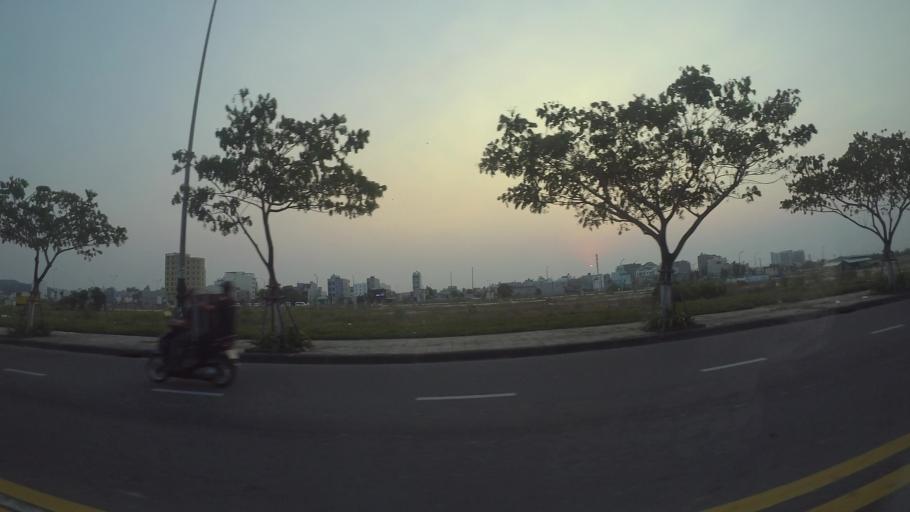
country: VN
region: Da Nang
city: Ngu Hanh Son
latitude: 16.0193
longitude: 108.2591
